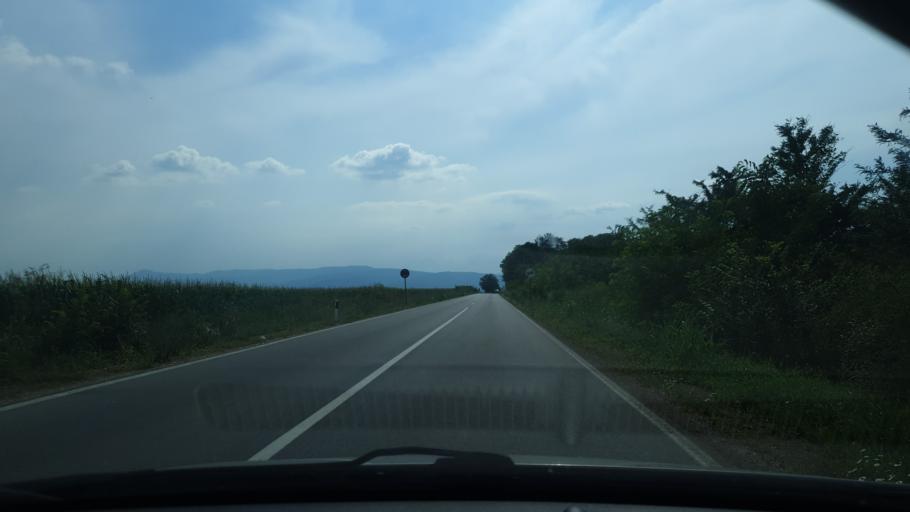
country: RS
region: Central Serbia
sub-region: Pomoravski Okrug
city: Cuprija
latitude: 43.9431
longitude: 21.4154
